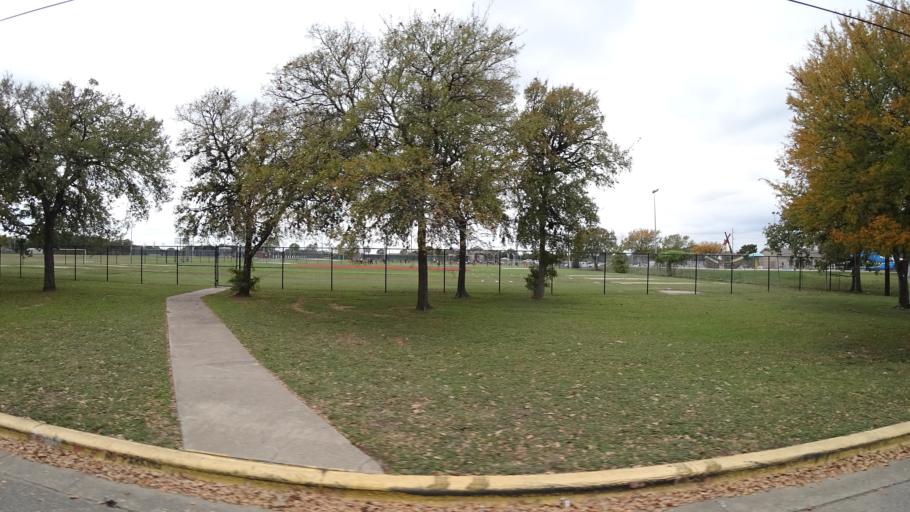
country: US
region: Texas
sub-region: Williamson County
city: Round Rock
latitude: 30.5068
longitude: -97.6975
